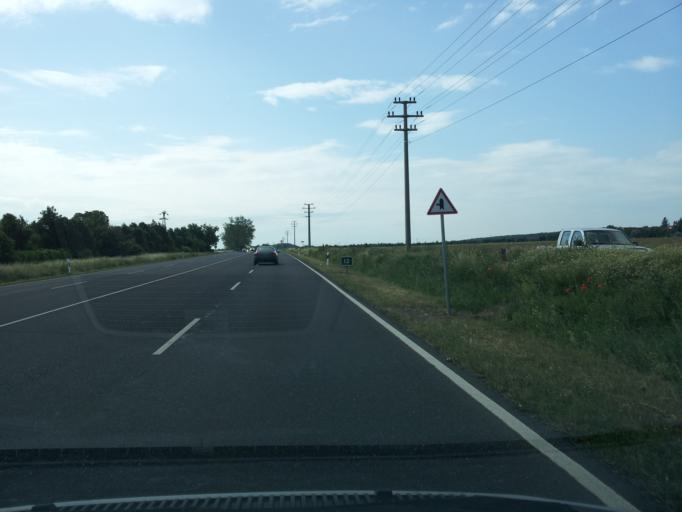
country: HU
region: Veszprem
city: Veszprem
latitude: 47.0666
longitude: 17.9215
